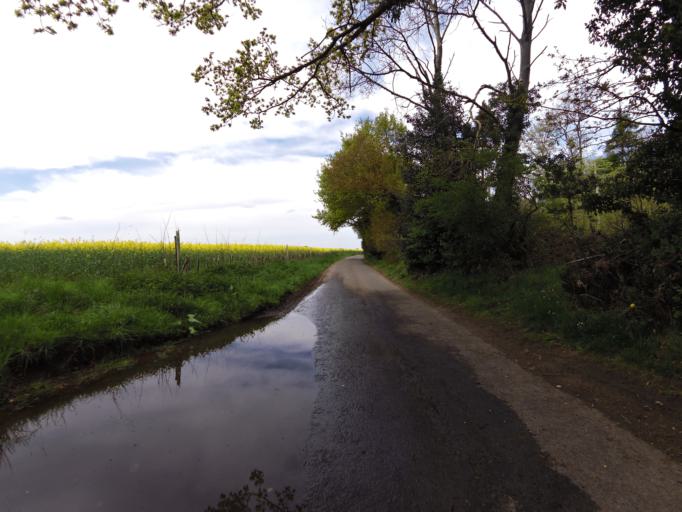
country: GB
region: England
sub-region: Essex
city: Mistley
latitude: 51.9914
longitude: 1.1326
